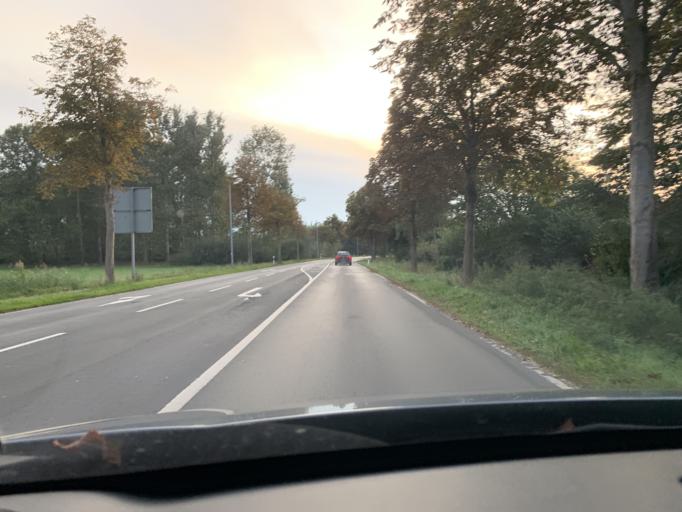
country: DE
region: Lower Saxony
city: Westerstede
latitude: 53.2499
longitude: 7.9263
